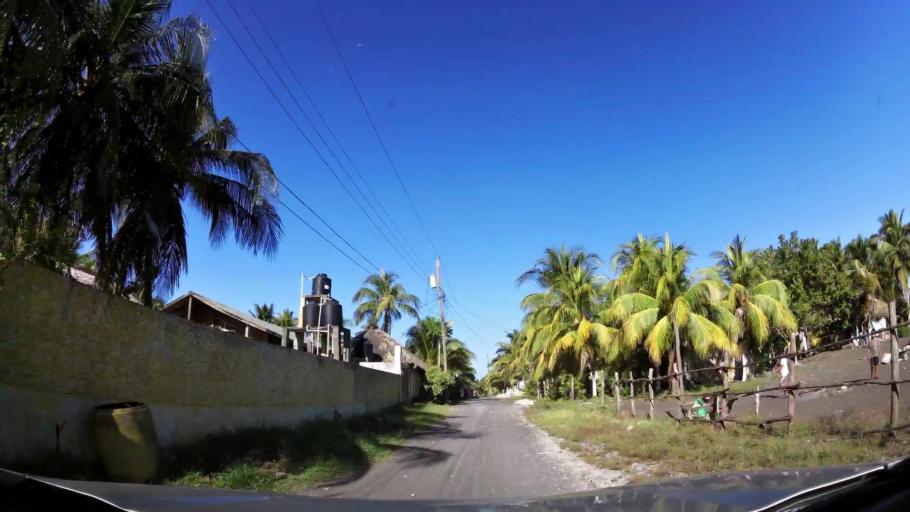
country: GT
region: Santa Rosa
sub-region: Municipio de Taxisco
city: Taxisco
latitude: 13.8916
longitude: -90.4875
